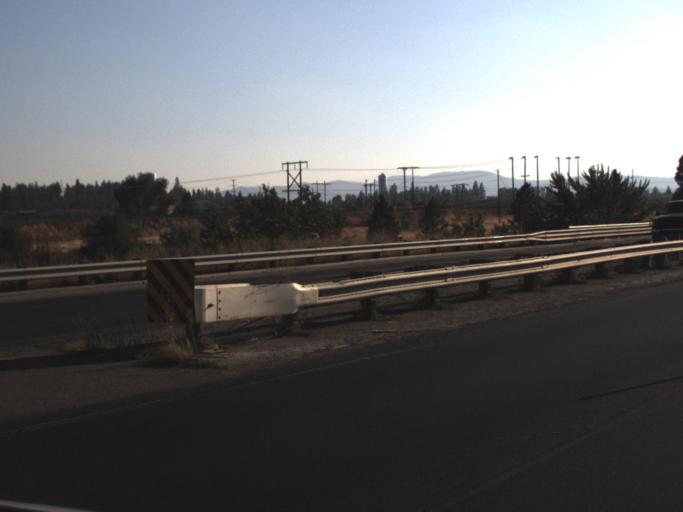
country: US
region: Washington
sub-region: Spokane County
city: Spokane Valley
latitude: 47.6923
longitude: -117.2338
